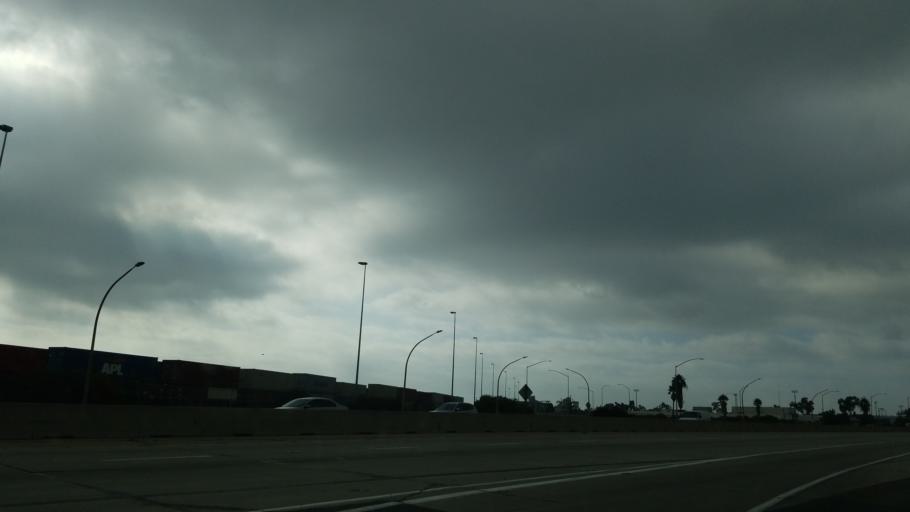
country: US
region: California
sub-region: Los Angeles County
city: San Pedro
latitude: 33.7515
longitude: -118.2575
